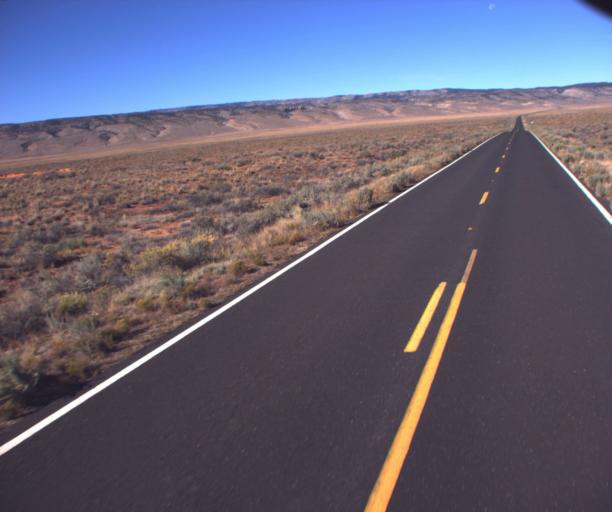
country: US
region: Arizona
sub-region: Coconino County
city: Page
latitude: 36.7138
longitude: -111.9850
